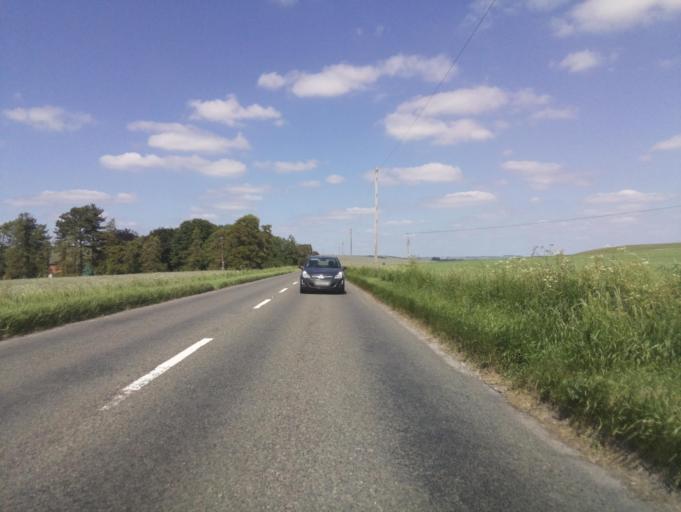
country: GB
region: England
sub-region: Wiltshire
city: Avebury
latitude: 51.3982
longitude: -1.9331
